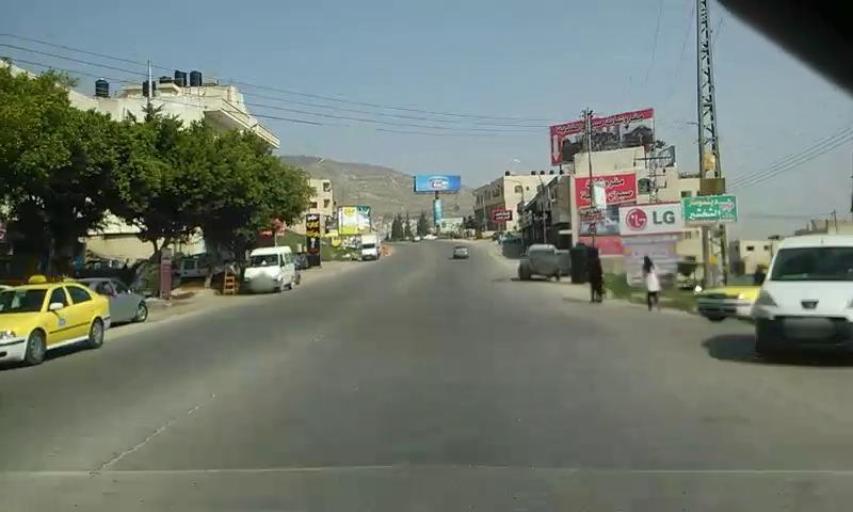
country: PS
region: West Bank
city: Kafr Qallil
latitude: 32.2019
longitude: 35.2851
